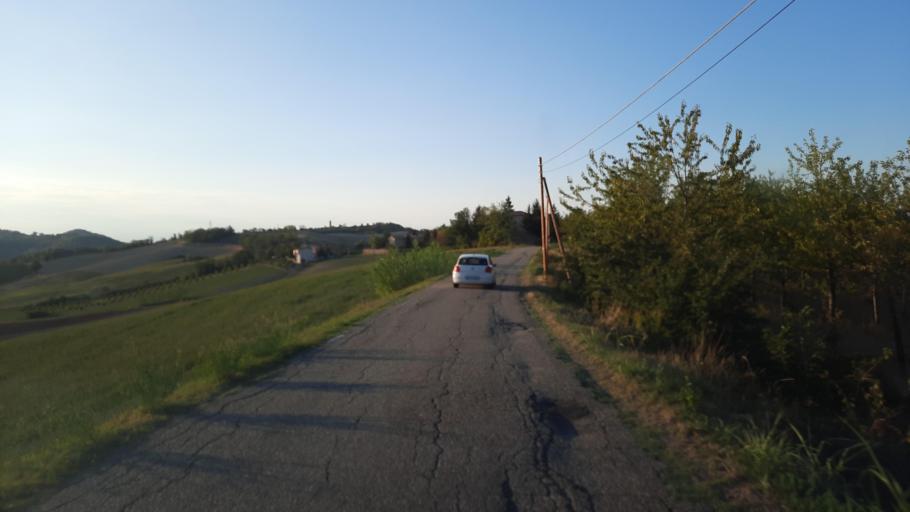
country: IT
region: Piedmont
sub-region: Provincia di Alessandria
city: Cereseto
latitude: 45.0720
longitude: 8.3286
